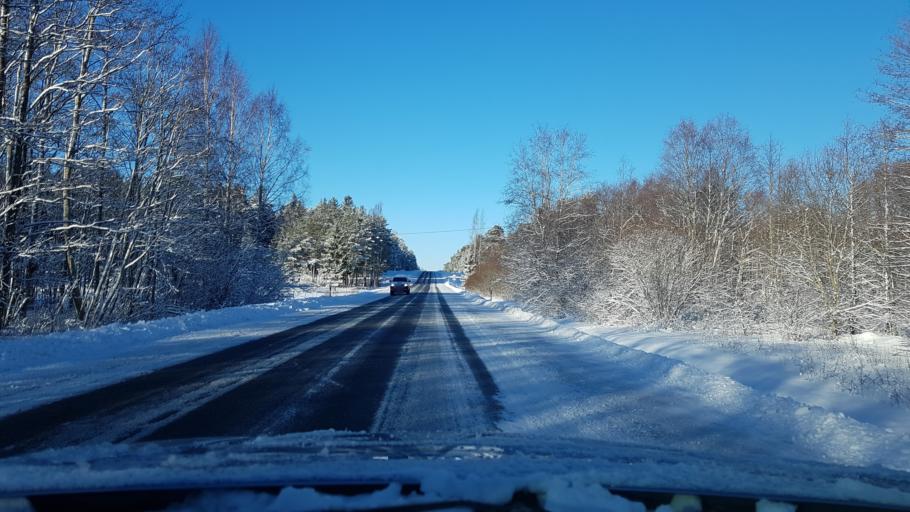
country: EE
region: Hiiumaa
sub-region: Kaerdla linn
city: Kardla
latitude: 58.9579
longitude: 22.8592
